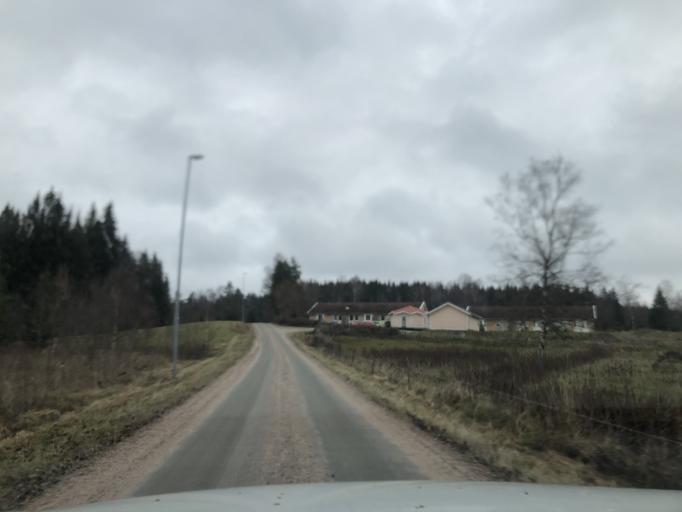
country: SE
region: Vaestra Goetaland
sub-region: Ulricehamns Kommun
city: Ulricehamn
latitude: 57.8664
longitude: 13.5547
